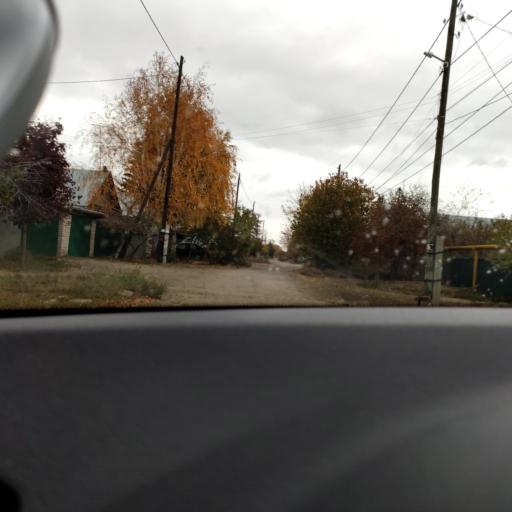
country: RU
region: Samara
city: Smyshlyayevka
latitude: 53.2379
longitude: 50.3243
